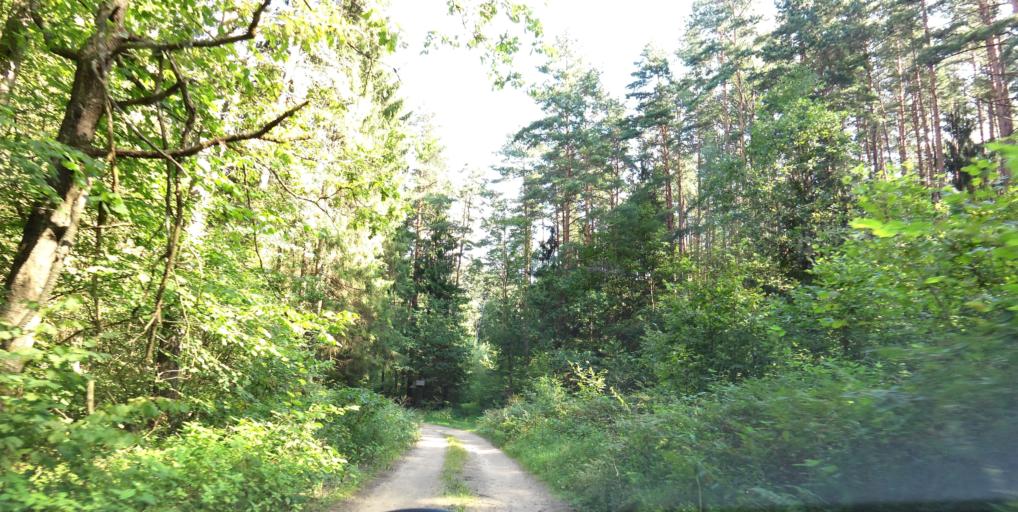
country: LT
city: Grigiskes
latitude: 54.7381
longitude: 25.0396
